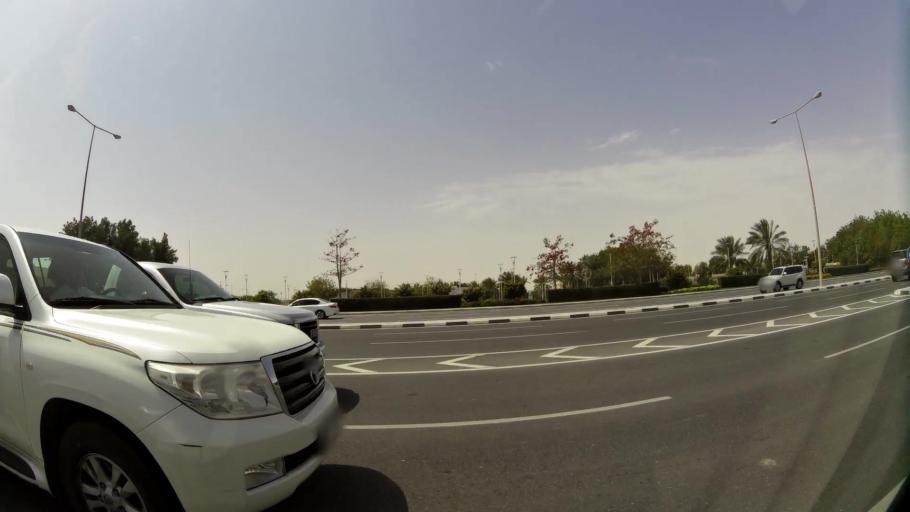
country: QA
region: Baladiyat ad Dawhah
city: Doha
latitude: 25.3335
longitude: 51.4822
